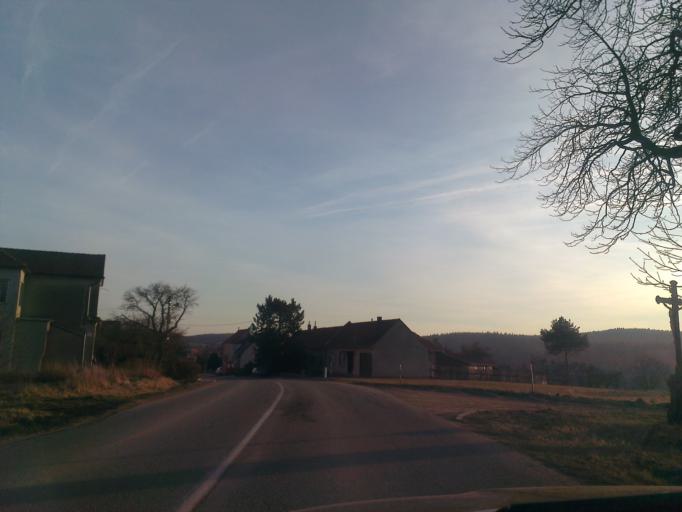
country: CZ
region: South Moravian
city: Bilovice nad Svitavou
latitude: 49.2604
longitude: 16.7300
